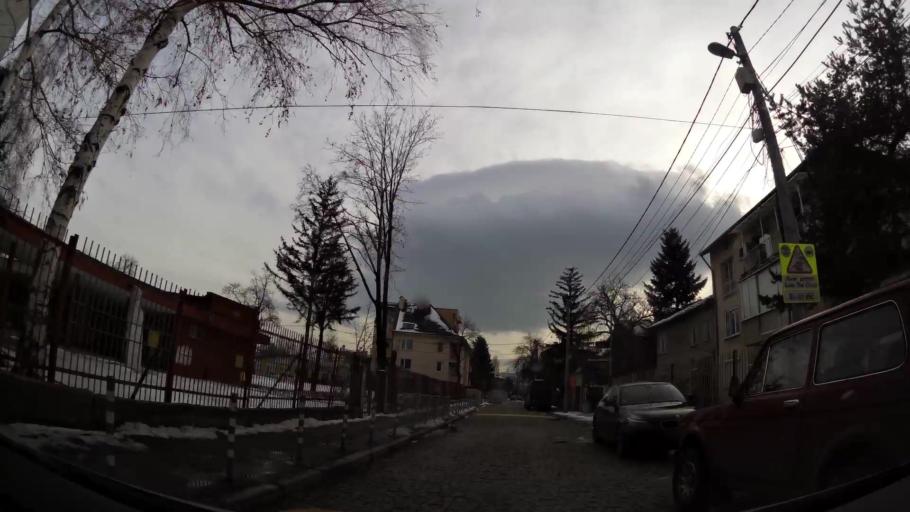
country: BG
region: Sofia-Capital
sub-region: Stolichna Obshtina
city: Sofia
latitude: 42.6978
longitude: 23.3708
